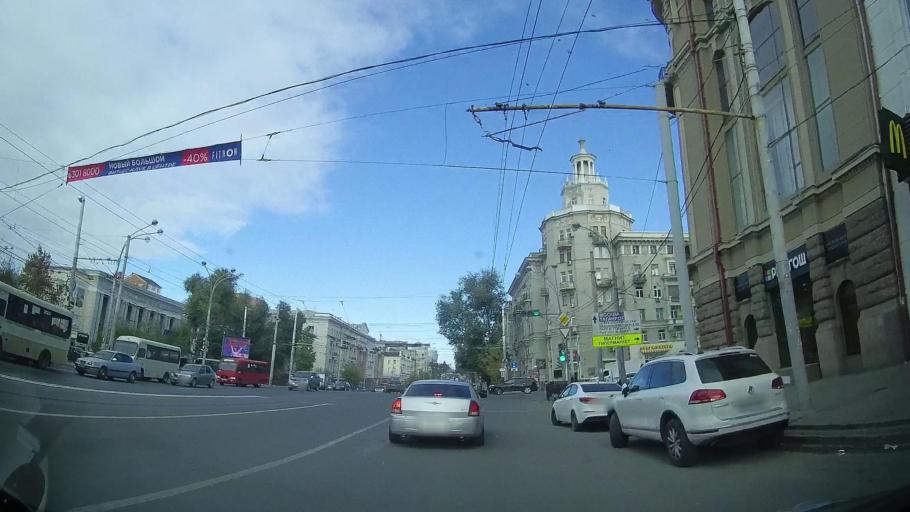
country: RU
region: Rostov
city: Rostov-na-Donu
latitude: 47.2196
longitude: 39.7079
